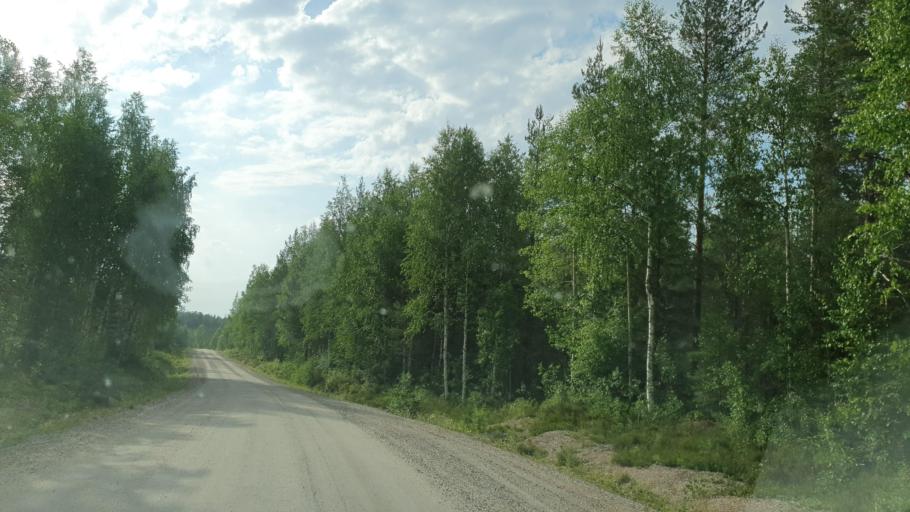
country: FI
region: Kainuu
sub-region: Kehys-Kainuu
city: Kuhmo
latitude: 64.0740
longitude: 29.7269
